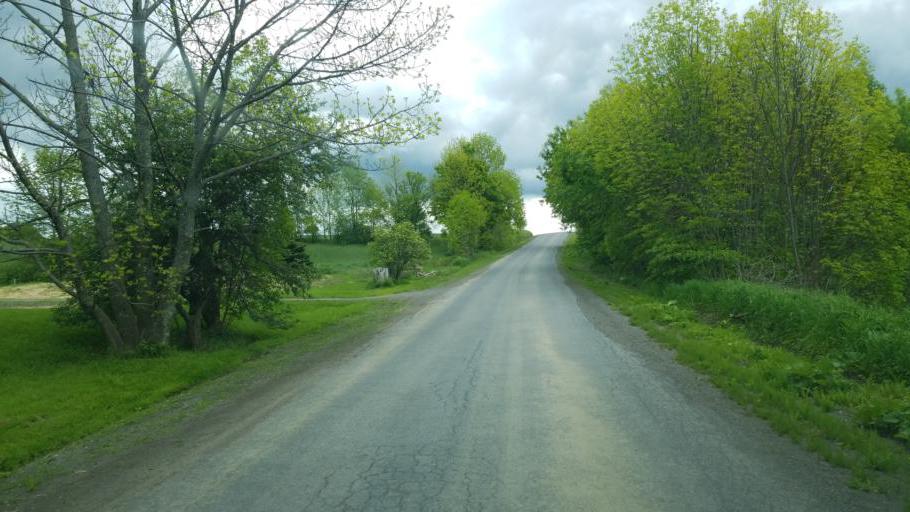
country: US
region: New York
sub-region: Otsego County
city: Richfield Springs
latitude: 42.8423
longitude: -75.1696
